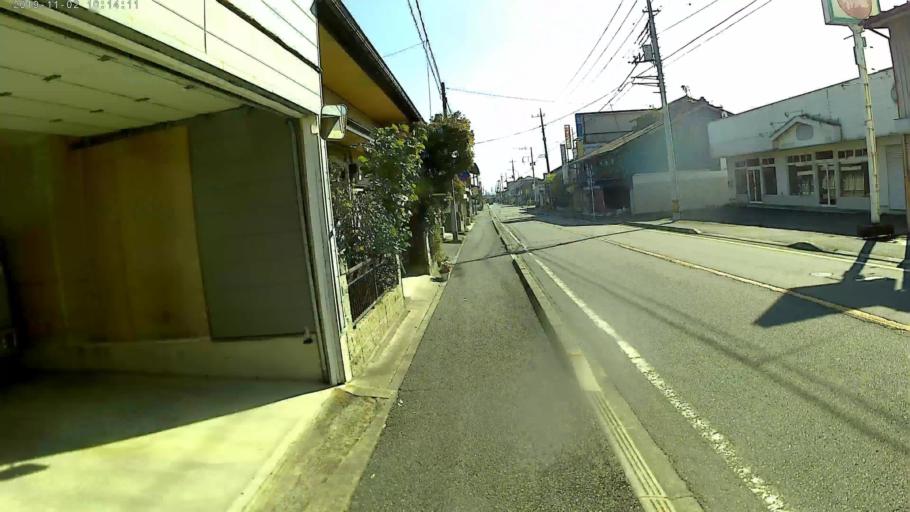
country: JP
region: Gunma
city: Annaka
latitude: 36.3161
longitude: 138.7936
